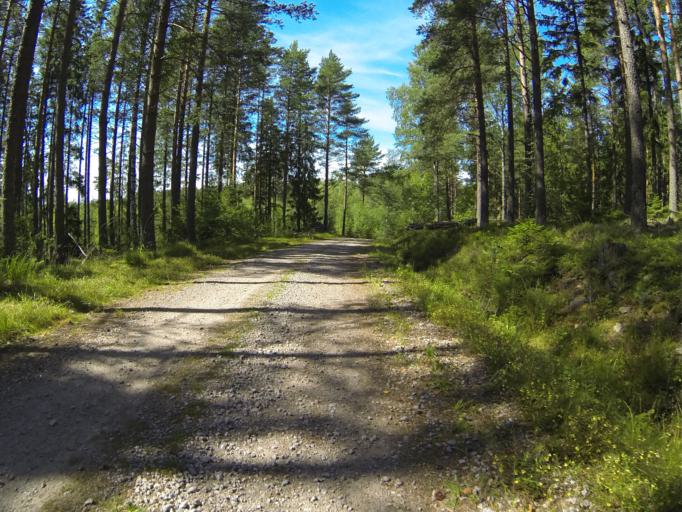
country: FI
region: Varsinais-Suomi
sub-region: Salo
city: Pernioe
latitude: 60.2849
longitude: 23.0717
